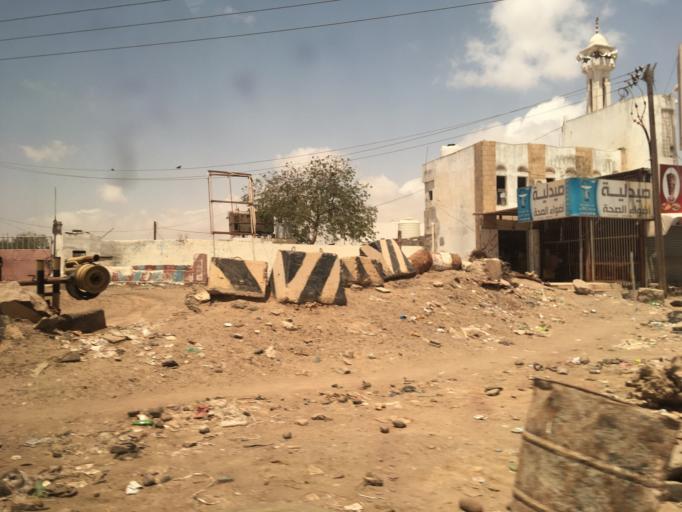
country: YE
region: Aden
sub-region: Al Mansura
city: Al Mansurah
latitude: 12.8720
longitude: 44.9729
